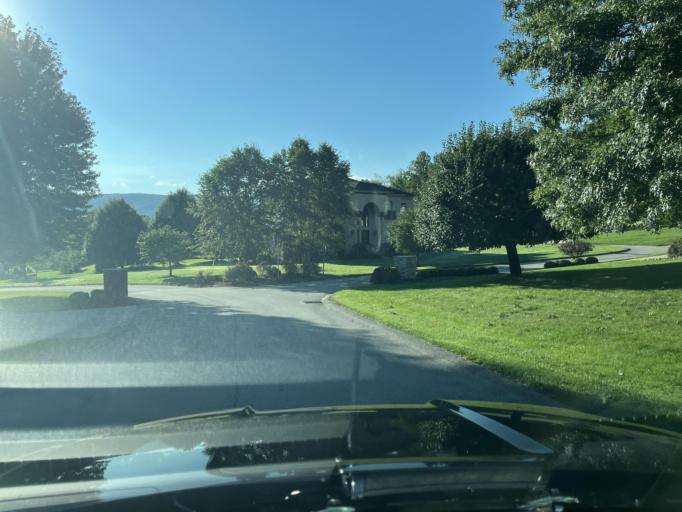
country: US
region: Pennsylvania
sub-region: Fayette County
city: Leith-Hatfield
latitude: 39.8763
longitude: -79.7378
